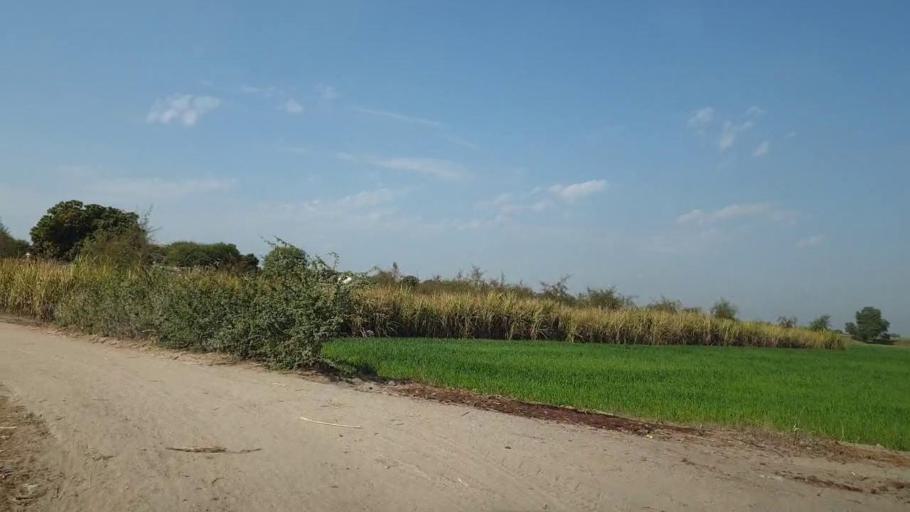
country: PK
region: Sindh
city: Matiari
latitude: 25.5709
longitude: 68.5883
